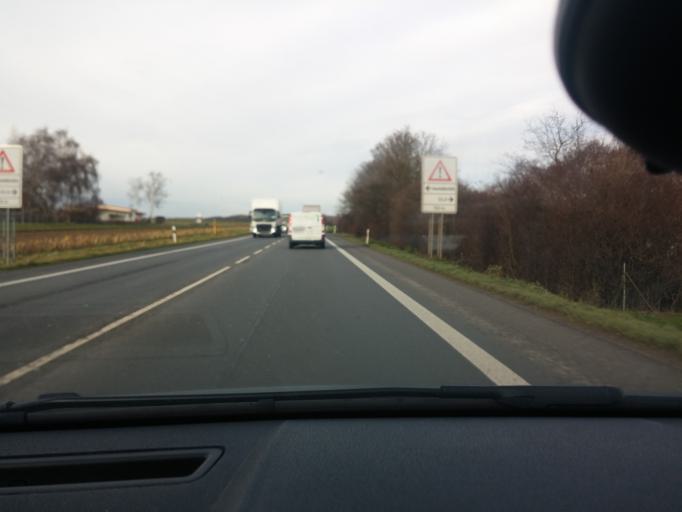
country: DE
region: Hesse
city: Gross-Umstadt
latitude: 49.8740
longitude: 8.9108
